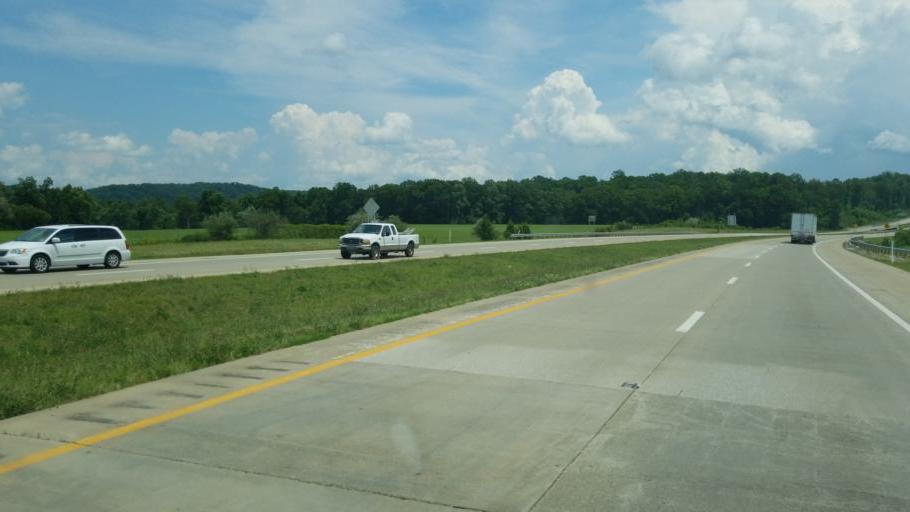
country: US
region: West Virginia
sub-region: Putnam County
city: Eleanor
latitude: 38.5479
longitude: -81.9779
